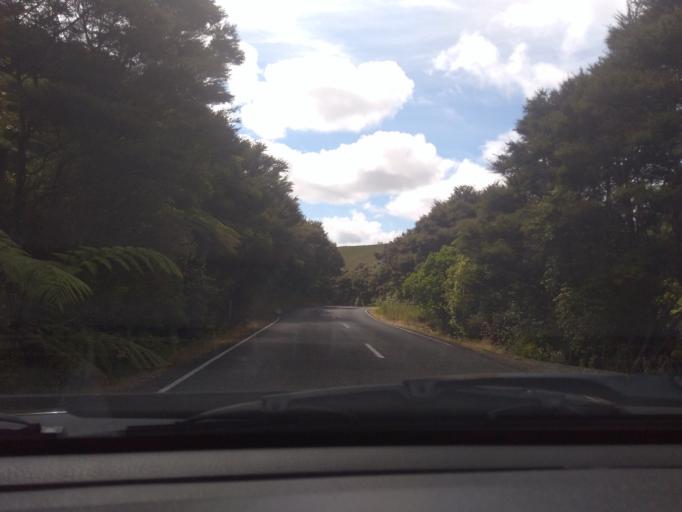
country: NZ
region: Northland
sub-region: Far North District
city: Taipa
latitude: -34.9863
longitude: 173.7009
